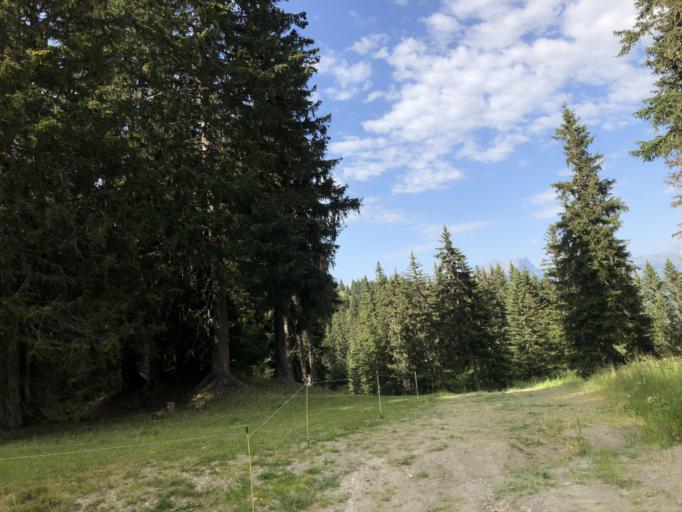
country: FR
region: Rhone-Alpes
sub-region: Departement de la Haute-Savoie
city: Combloux
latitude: 45.8596
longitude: 6.6687
